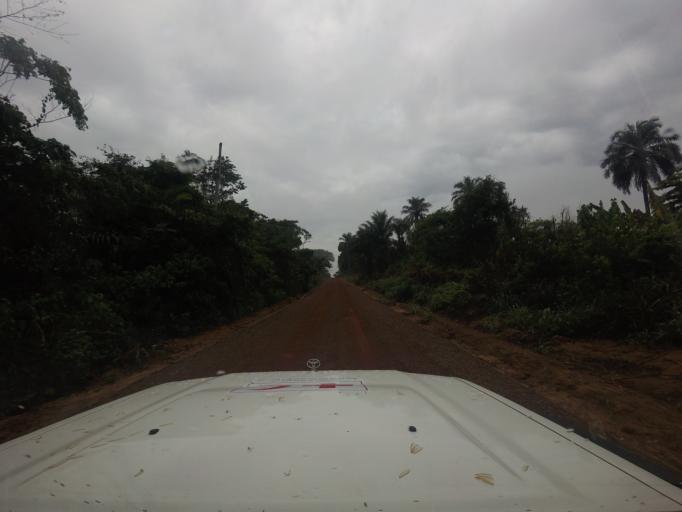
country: LR
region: Lofa
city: Voinjama
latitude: 8.3774
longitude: -9.8496
